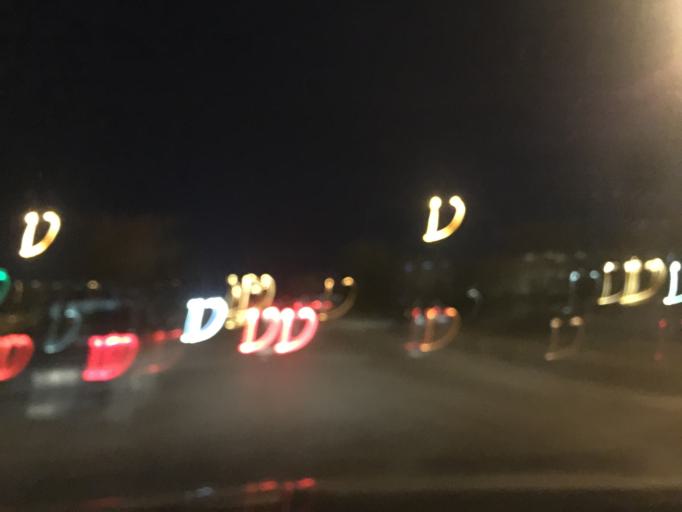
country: JO
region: Amman
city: Al Jubayhah
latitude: 32.0286
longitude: 35.8918
